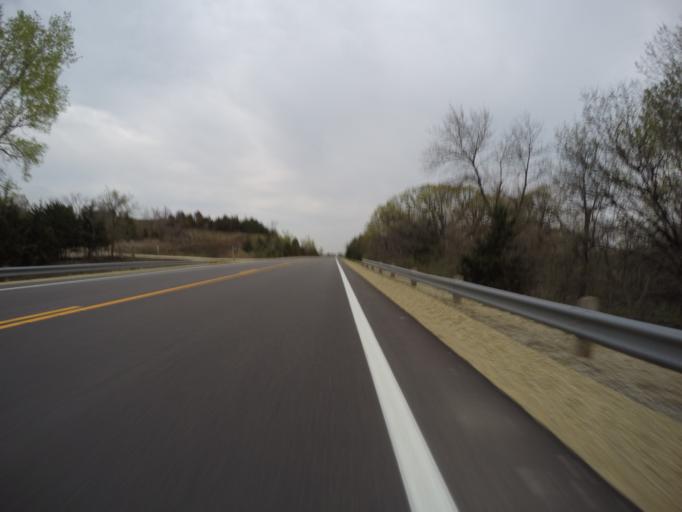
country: US
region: Kansas
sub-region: Riley County
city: Manhattan
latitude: 39.2975
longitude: -96.5567
